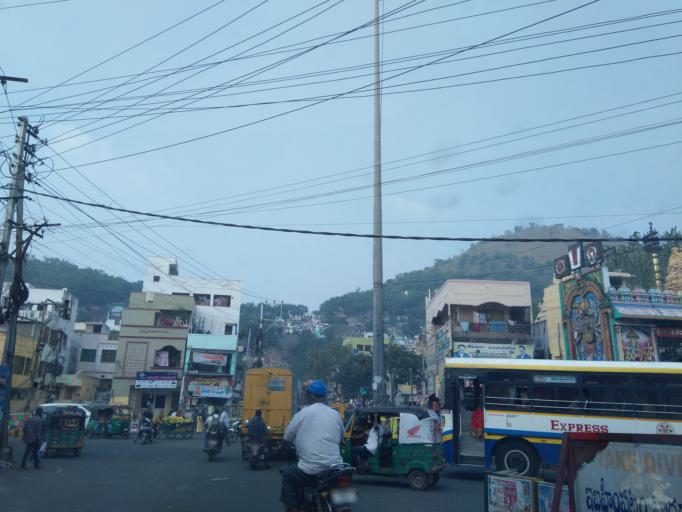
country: IN
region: Andhra Pradesh
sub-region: Krishna
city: Vijayawada
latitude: 16.5305
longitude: 80.6126
